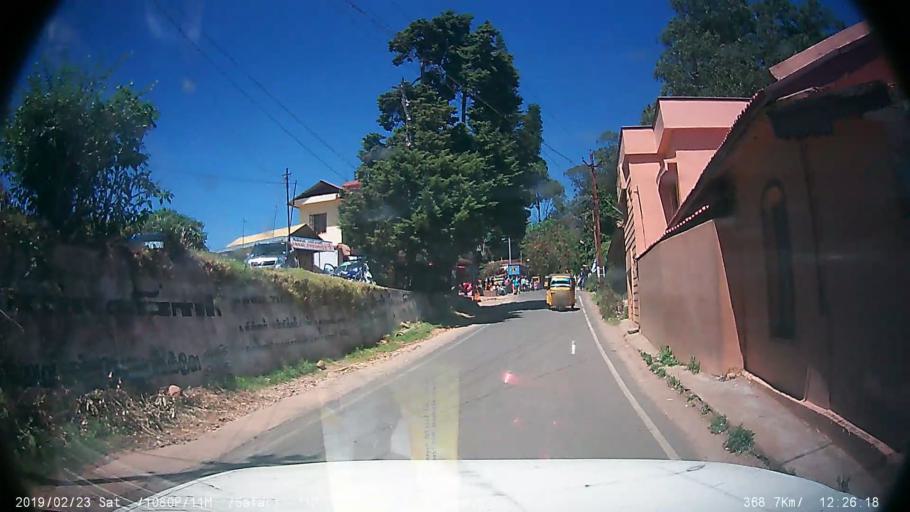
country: IN
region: Tamil Nadu
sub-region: Nilgiri
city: Wellington
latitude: 11.3435
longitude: 76.7882
